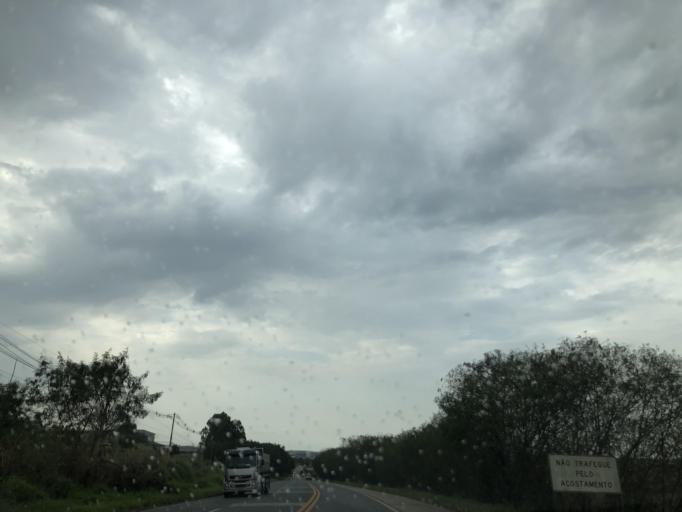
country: BR
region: Sao Paulo
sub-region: Salto De Pirapora
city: Salto de Pirapora
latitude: -23.6554
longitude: -47.5870
